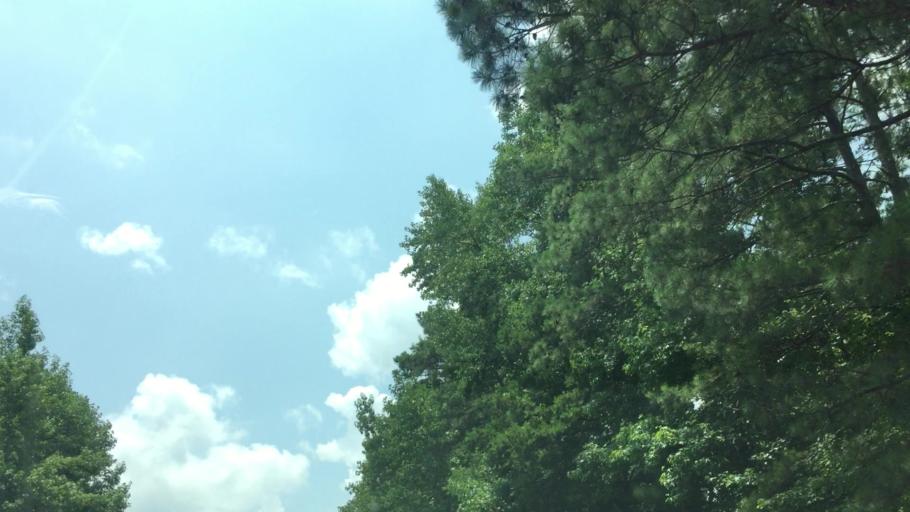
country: US
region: Georgia
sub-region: Carroll County
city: Carrollton
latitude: 33.6132
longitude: -84.9607
